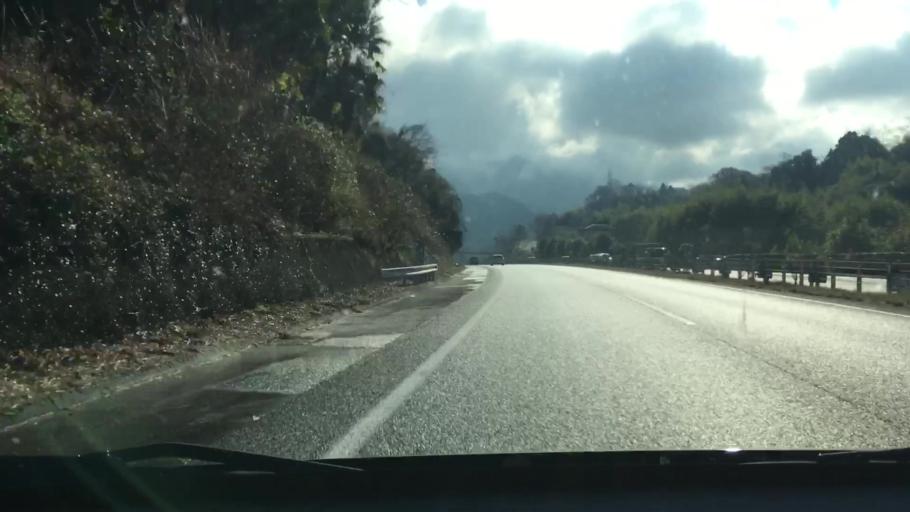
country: JP
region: Kumamoto
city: Matsubase
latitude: 32.5582
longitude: 130.6959
